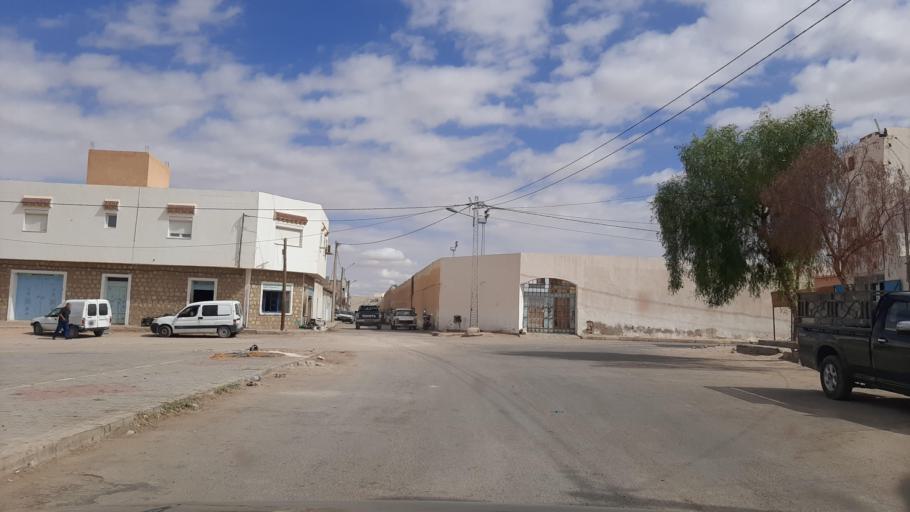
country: TN
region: Tataouine
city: Tataouine
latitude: 32.9271
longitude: 10.4415
